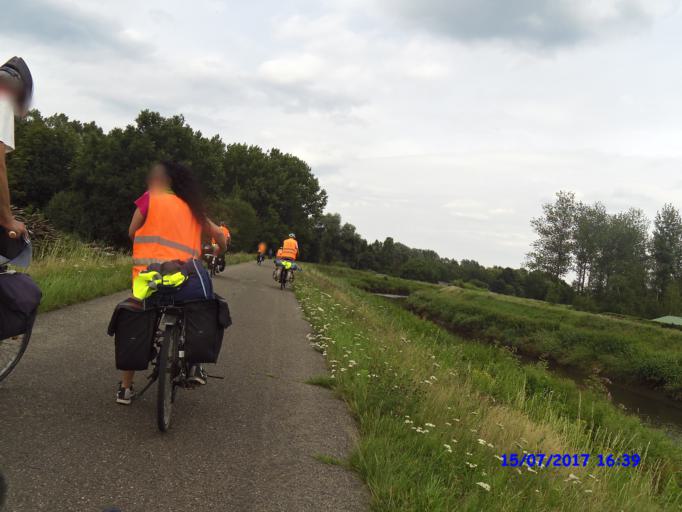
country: BE
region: Flanders
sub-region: Provincie Antwerpen
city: Nijlen
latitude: 51.1750
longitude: 4.6405
